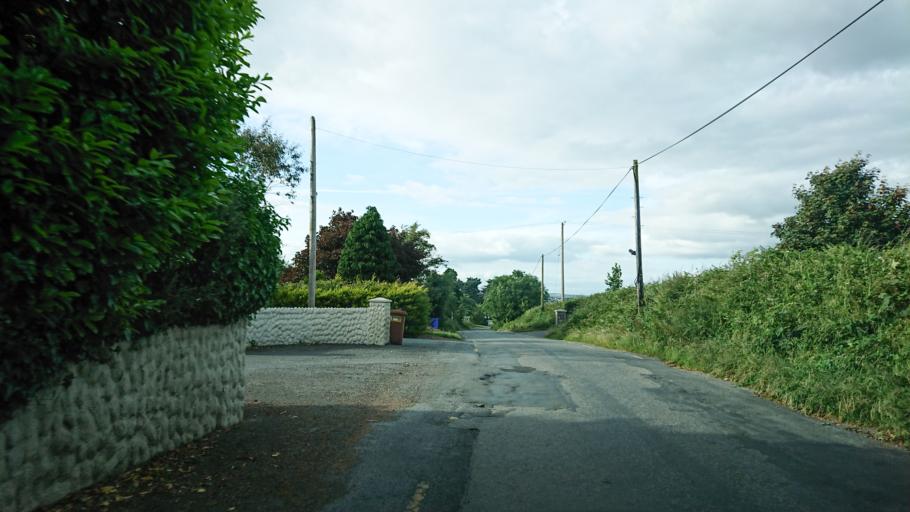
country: IE
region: Munster
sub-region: Waterford
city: Waterford
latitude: 52.2350
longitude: -7.1578
